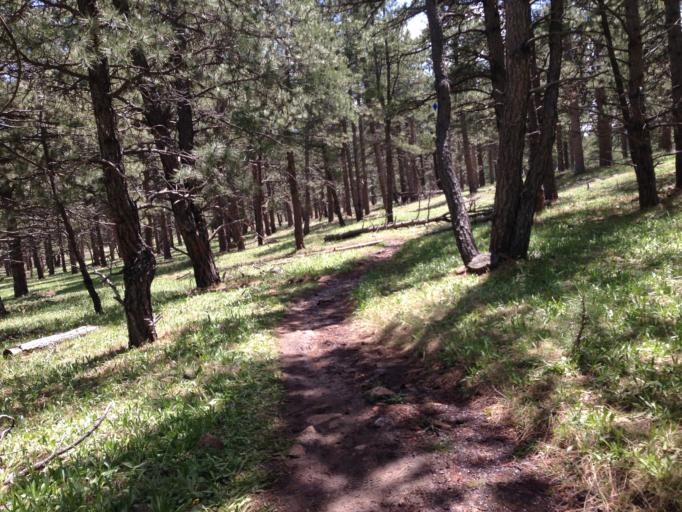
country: US
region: Colorado
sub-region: Boulder County
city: Boulder
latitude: 39.9159
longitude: -105.2714
